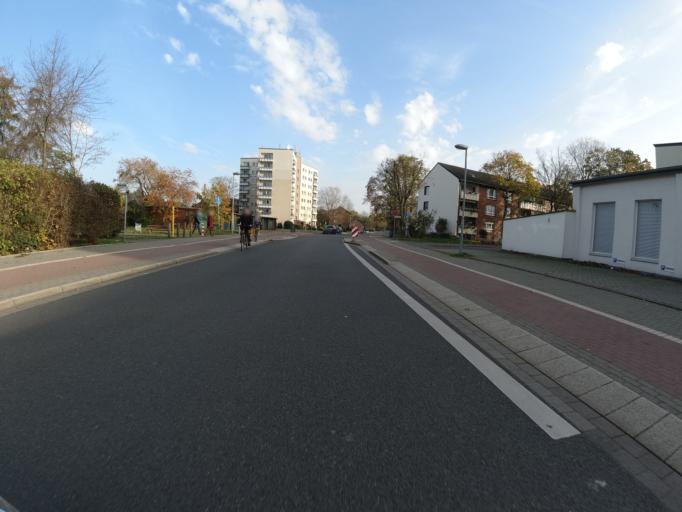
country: DE
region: North Rhine-Westphalia
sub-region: Regierungsbezirk Dusseldorf
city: Moers
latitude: 51.4480
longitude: 6.6126
